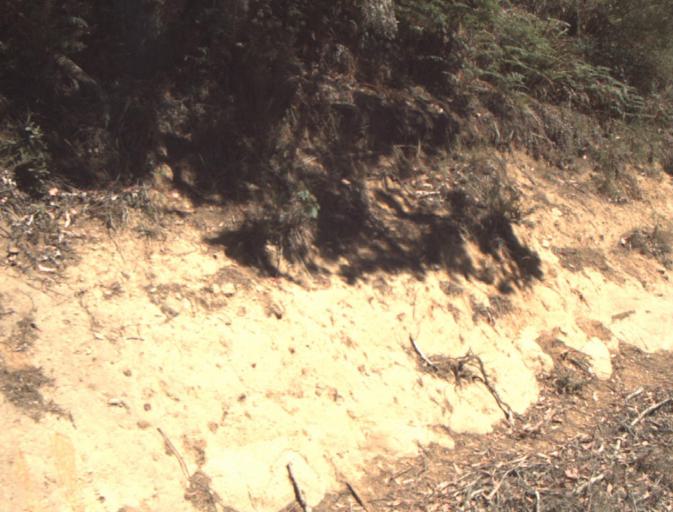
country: AU
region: Tasmania
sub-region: Dorset
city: Scottsdale
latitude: -41.3181
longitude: 147.4628
